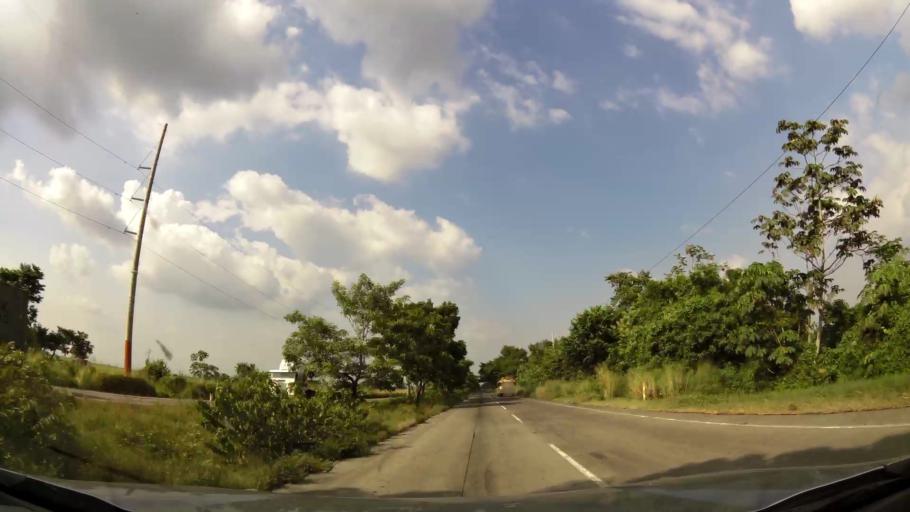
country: GT
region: Escuintla
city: Puerto San Jose
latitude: 14.0608
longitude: -90.7761
